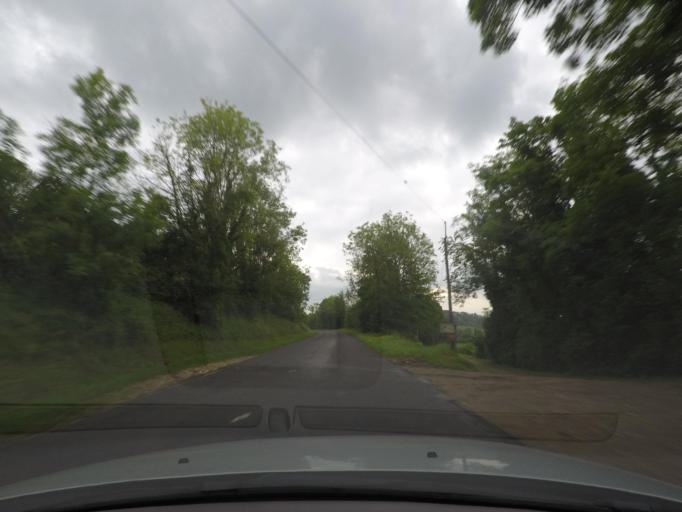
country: FR
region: Haute-Normandie
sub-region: Departement de la Seine-Maritime
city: Neufchatel-en-Bray
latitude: 49.7349
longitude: 1.4704
